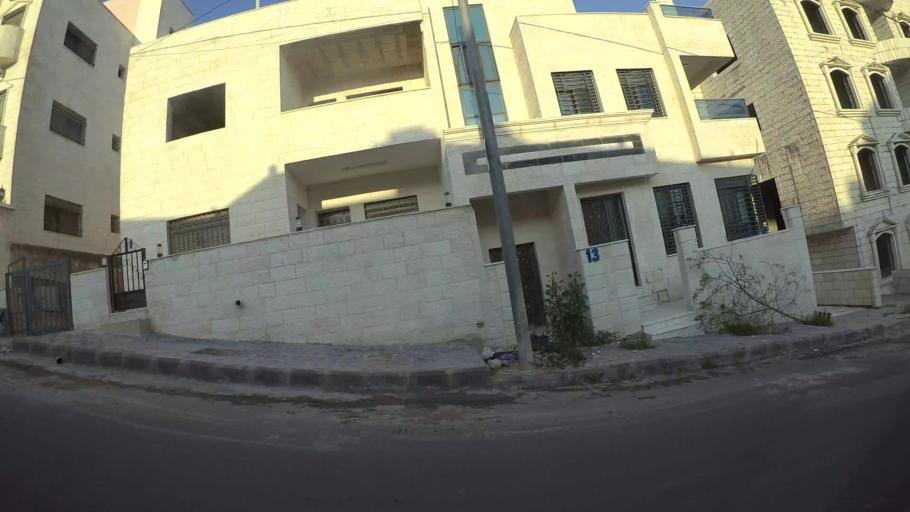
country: JO
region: Amman
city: Amman
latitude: 31.9844
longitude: 35.9626
